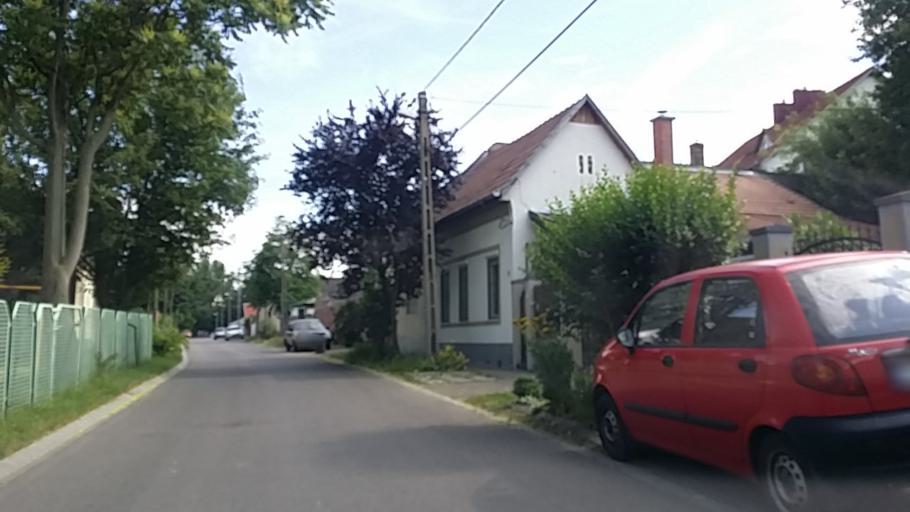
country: HU
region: Budapest
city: Budapest XXI. keruelet
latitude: 47.4296
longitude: 19.0812
